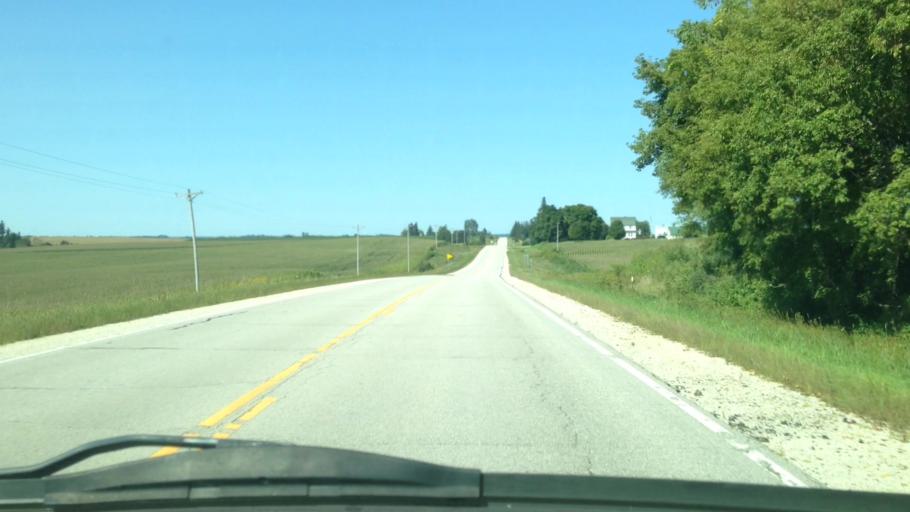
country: US
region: Minnesota
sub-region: Houston County
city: Spring Grove
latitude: 43.6087
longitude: -91.7903
